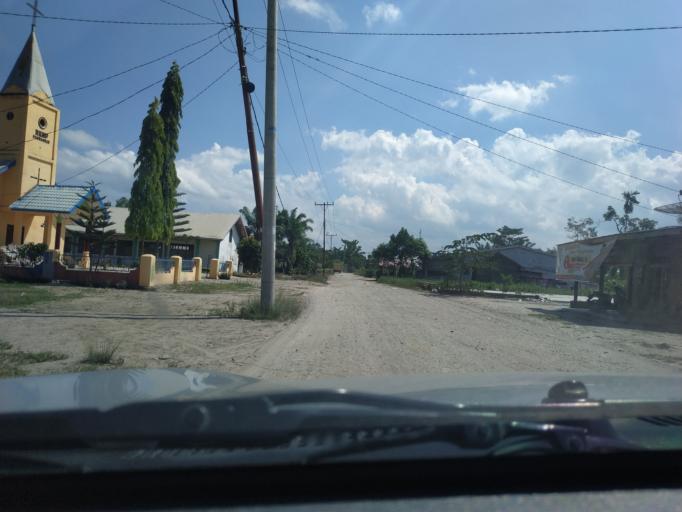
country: ID
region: North Sumatra
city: Tanjungbalai
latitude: 2.8799
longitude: 99.8615
